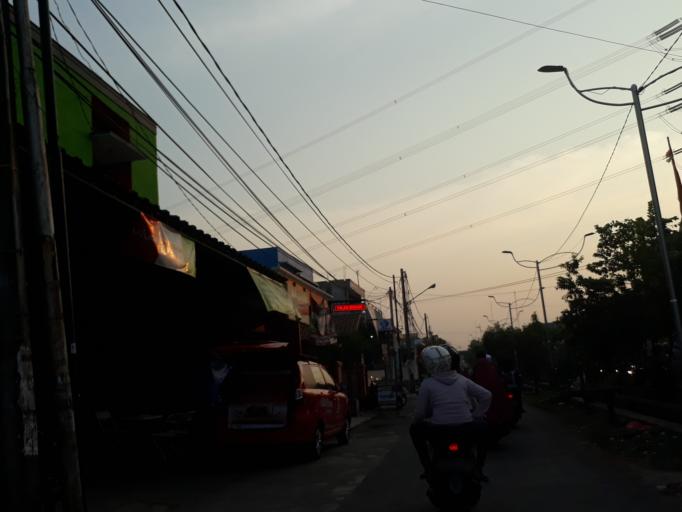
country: ID
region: West Java
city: Bekasi
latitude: -6.2434
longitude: 107.0490
